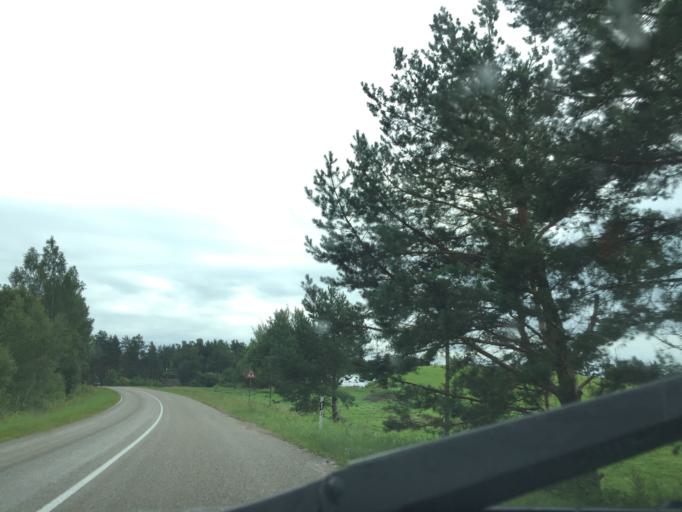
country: LV
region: Dagda
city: Dagda
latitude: 56.1983
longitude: 27.3247
